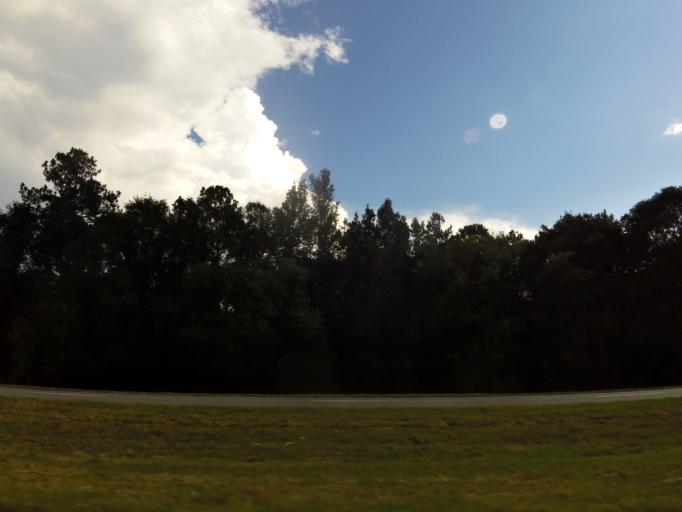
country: US
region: Georgia
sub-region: Brooks County
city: Quitman
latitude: 30.7927
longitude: -83.4634
